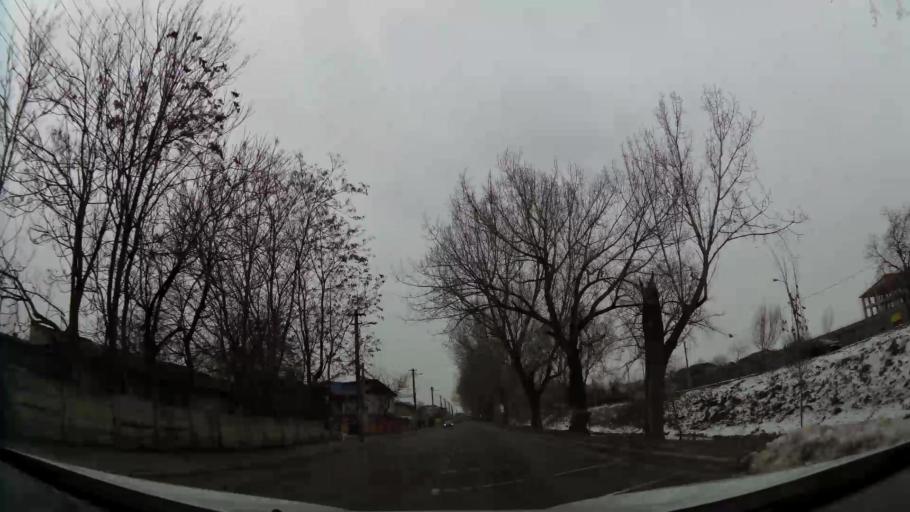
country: RO
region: Prahova
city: Ploiesti
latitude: 44.9454
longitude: 26.0408
